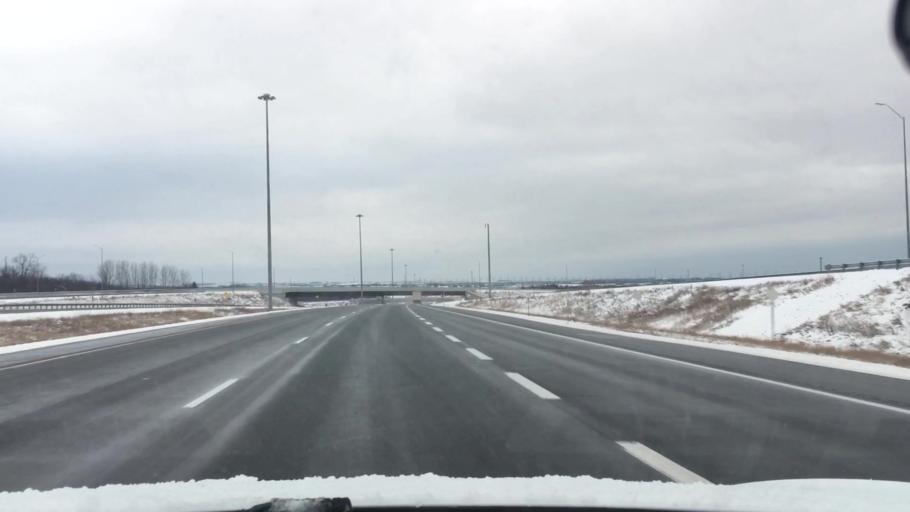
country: CA
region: Ontario
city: Ajax
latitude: 43.9531
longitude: -79.0150
